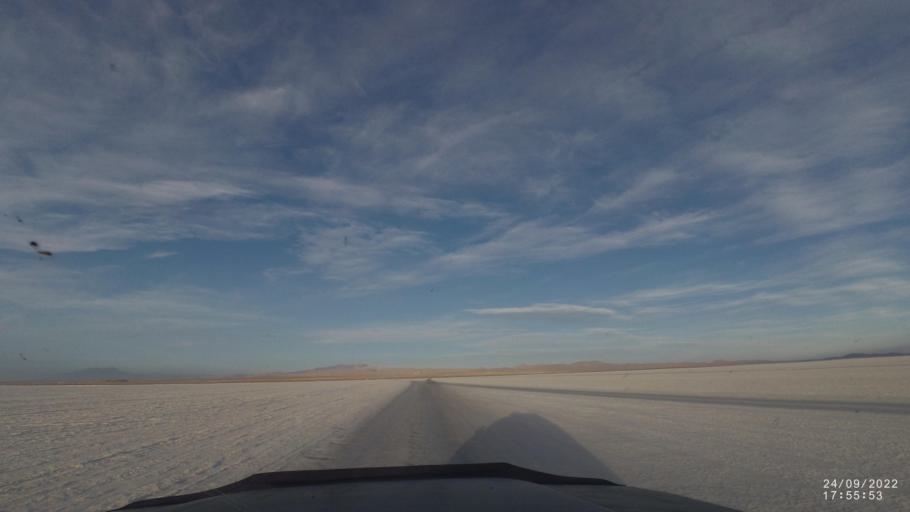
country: BO
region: Potosi
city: Colchani
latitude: -20.3260
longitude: -67.0233
